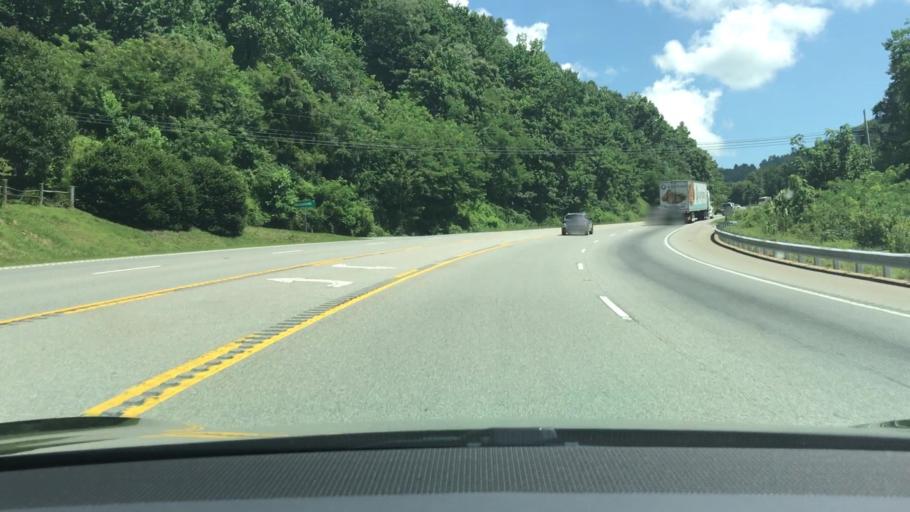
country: US
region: North Carolina
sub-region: Macon County
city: Franklin
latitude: 35.2461
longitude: -83.3206
